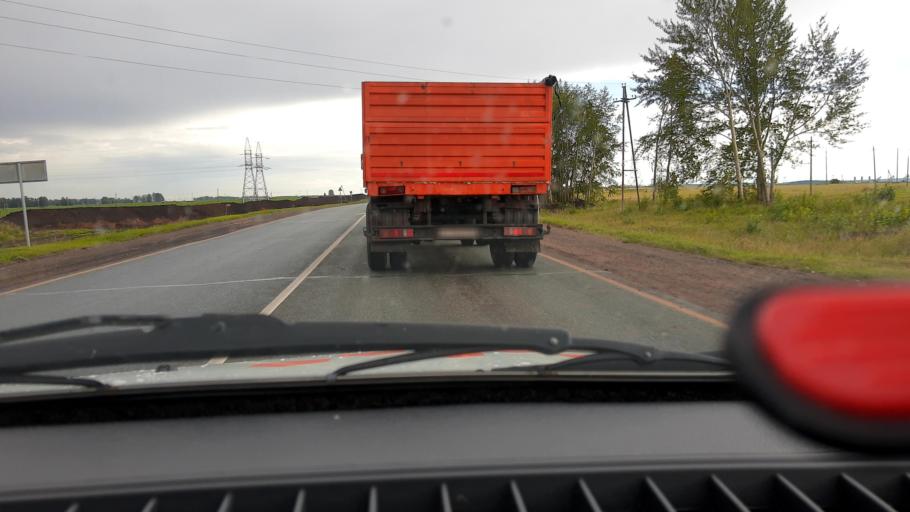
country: RU
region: Bashkortostan
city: Dyurtyuli
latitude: 55.3967
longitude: 54.8358
